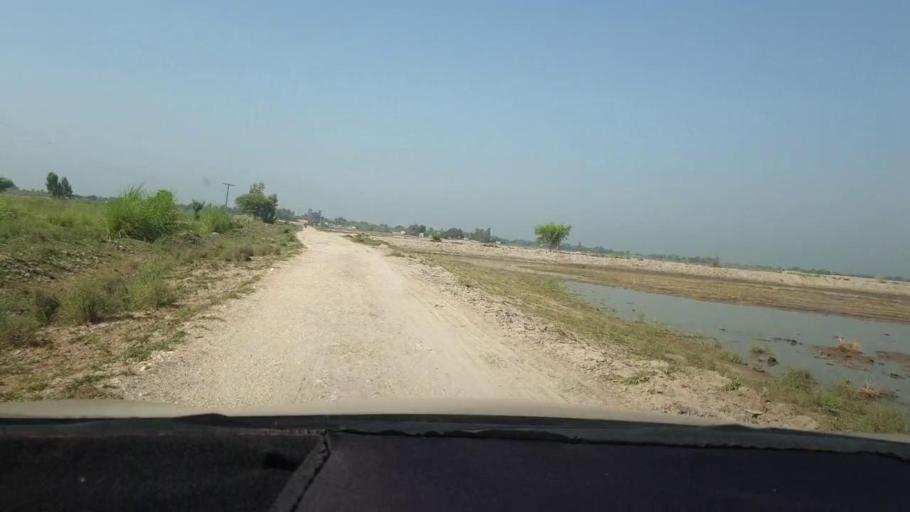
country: PK
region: Sindh
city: Miro Khan
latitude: 27.7115
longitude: 68.1018
